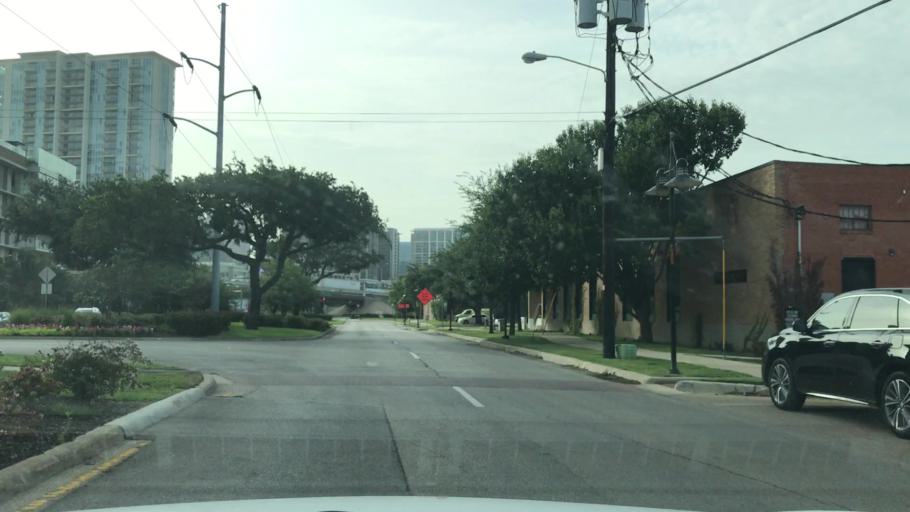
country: US
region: Texas
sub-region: Dallas County
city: Dallas
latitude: 32.7950
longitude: -96.8173
